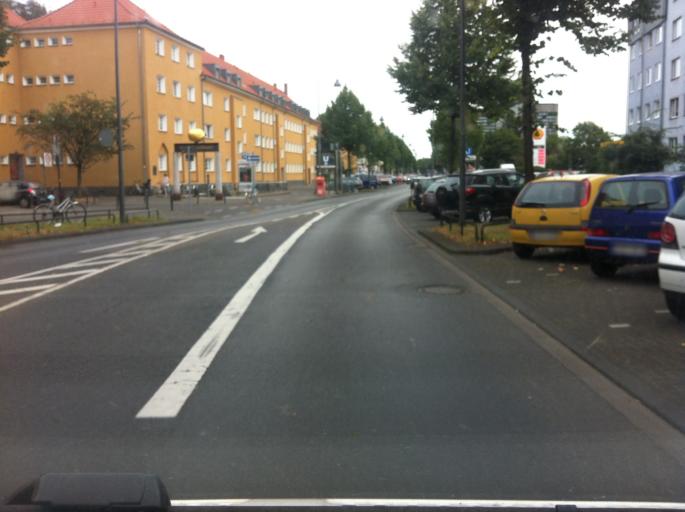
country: DE
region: North Rhine-Westphalia
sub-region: Regierungsbezirk Koln
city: Mengenich
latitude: 50.9609
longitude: 6.8932
